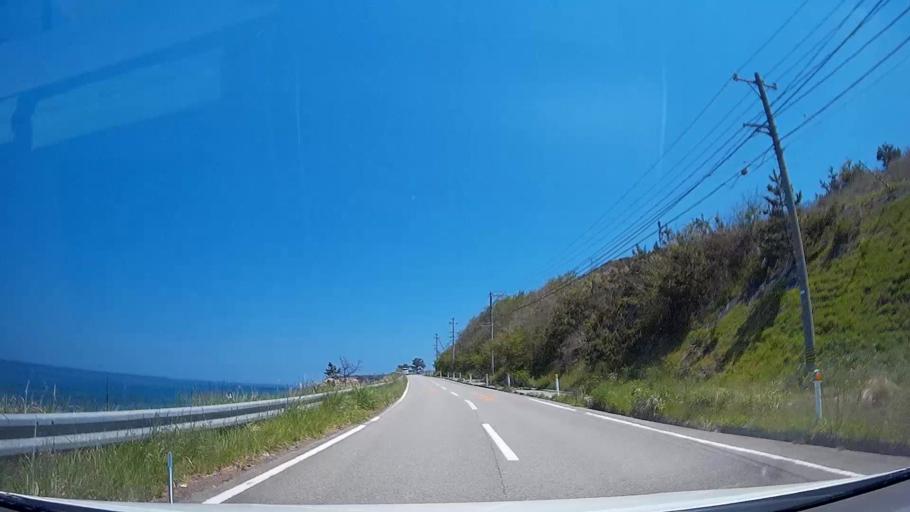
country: JP
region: Ishikawa
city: Nanao
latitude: 37.4373
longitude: 137.0365
